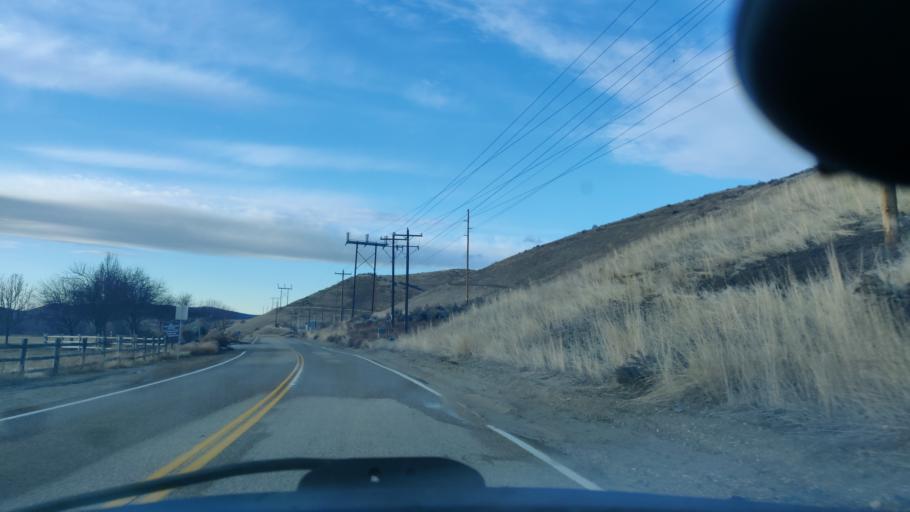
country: US
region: Idaho
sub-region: Ada County
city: Garden City
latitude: 43.7236
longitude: -116.2446
